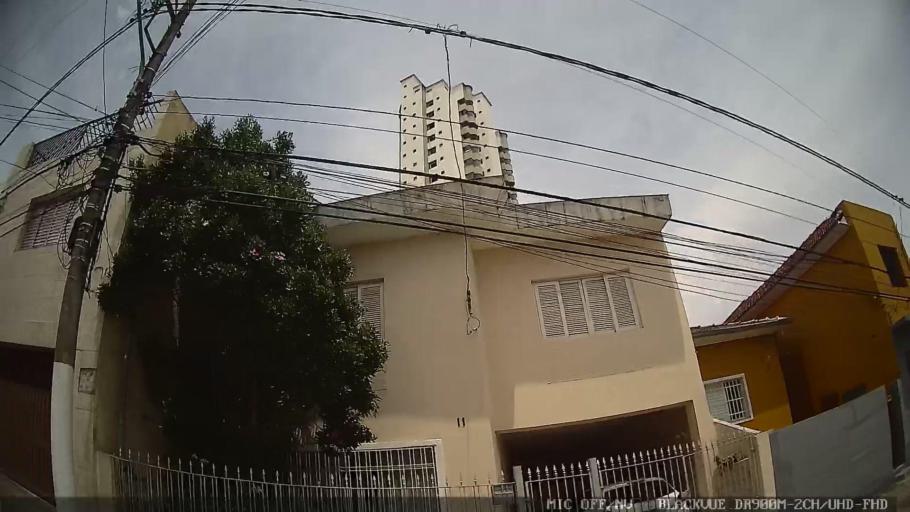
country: BR
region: Sao Paulo
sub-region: Sao Caetano Do Sul
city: Sao Caetano do Sul
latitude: -23.5690
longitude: -46.5646
